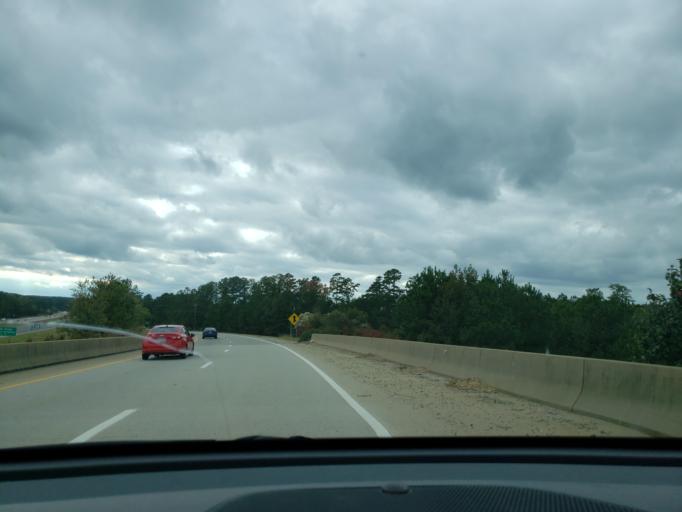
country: US
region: North Carolina
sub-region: Wake County
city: Morrisville
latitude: 35.9051
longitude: -78.7735
